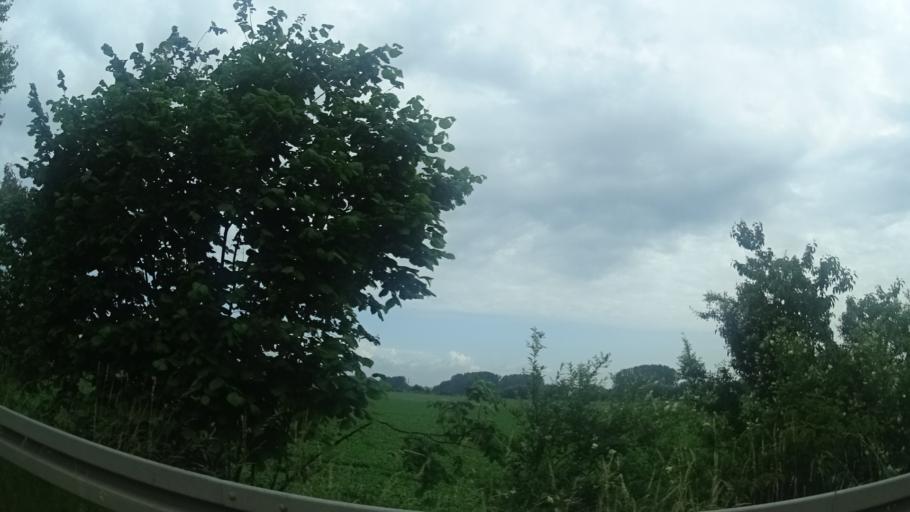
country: DE
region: Lower Saxony
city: Heyersum
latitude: 52.1608
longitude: 9.8558
